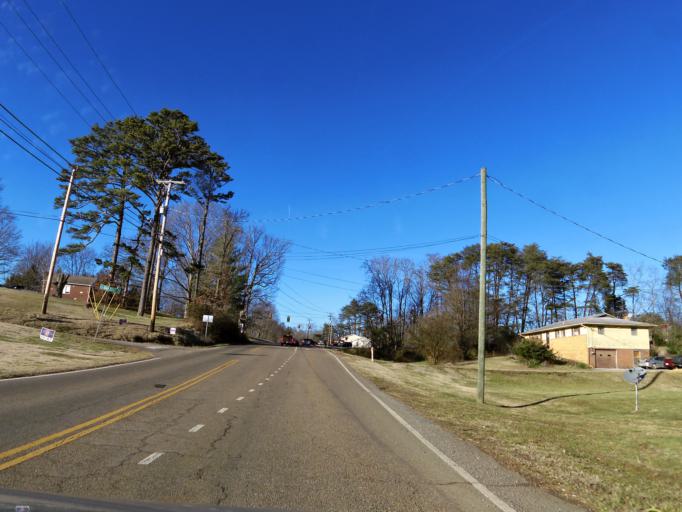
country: US
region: Tennessee
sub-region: Knox County
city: Knoxville
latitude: 35.8892
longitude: -83.9116
